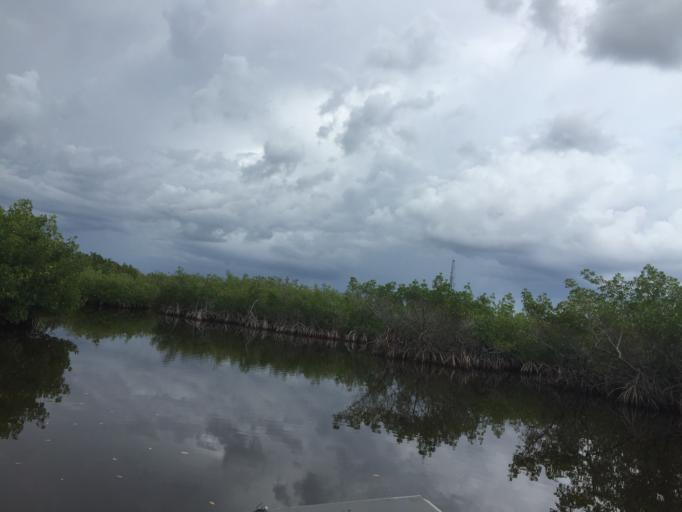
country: US
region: Florida
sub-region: Collier County
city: Marco
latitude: 25.9062
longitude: -81.3711
